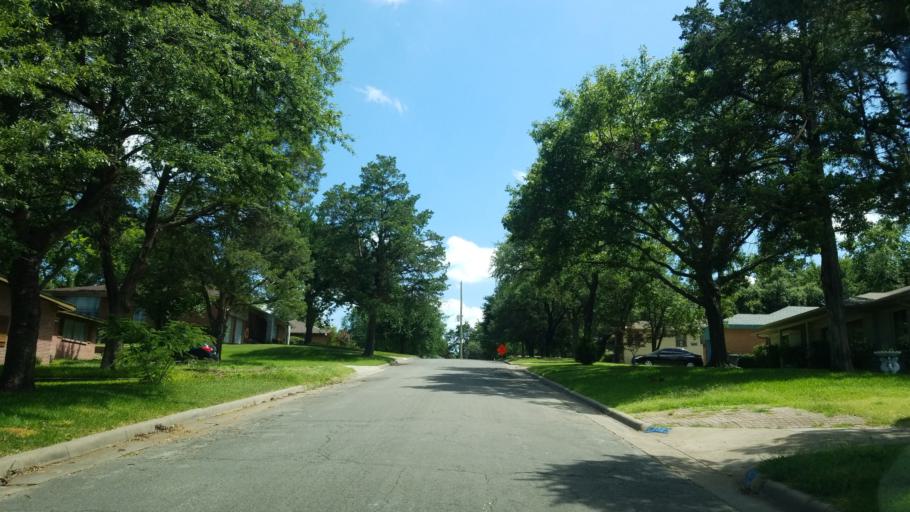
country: US
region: Texas
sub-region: Dallas County
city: Balch Springs
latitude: 32.7543
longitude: -96.6983
